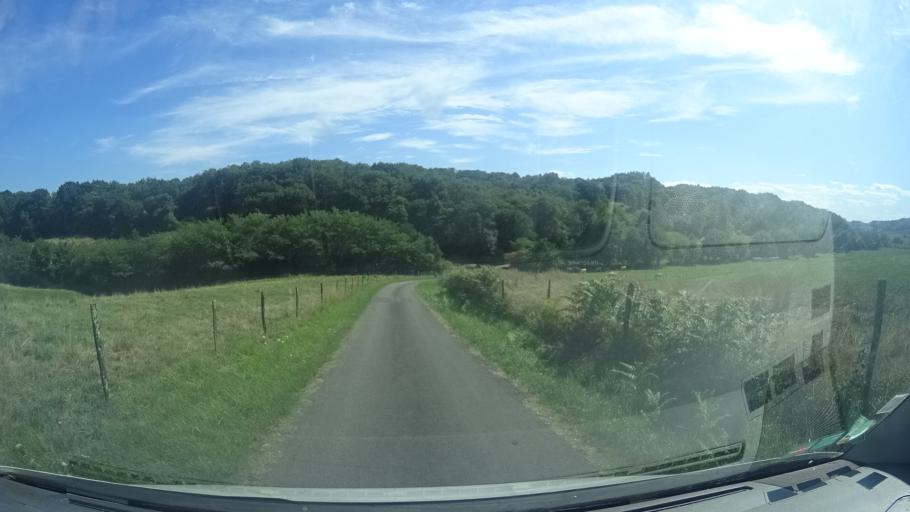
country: FR
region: Aquitaine
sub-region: Departement des Pyrenees-Atlantiques
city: Mont
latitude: 43.5037
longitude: -0.6897
